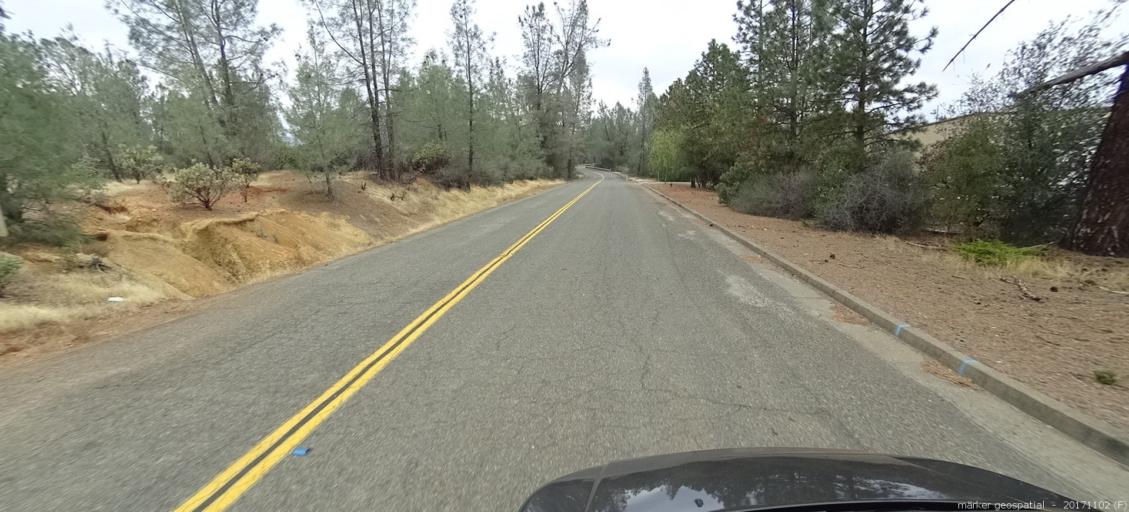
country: US
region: California
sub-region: Shasta County
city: Central Valley (historical)
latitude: 40.6610
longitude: -122.3954
